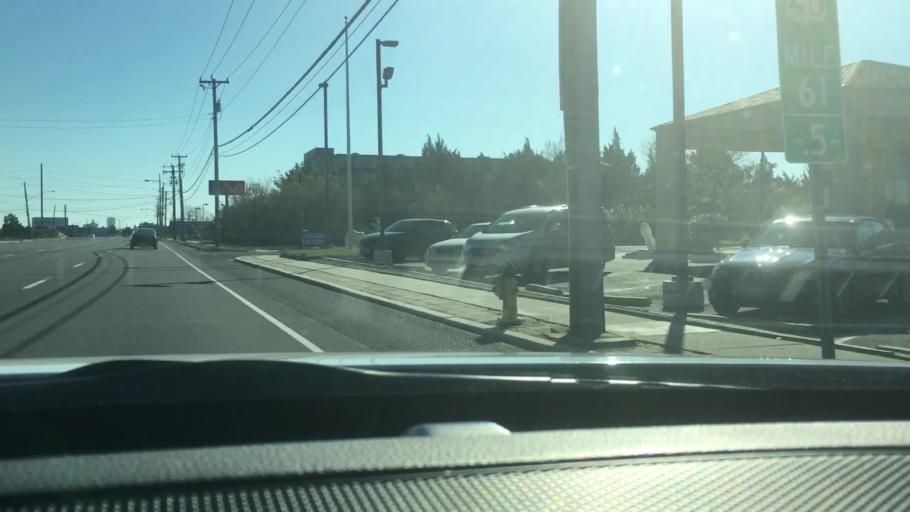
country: US
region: New Jersey
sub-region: Atlantic County
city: Pleasantville
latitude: 39.3785
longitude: -74.4903
